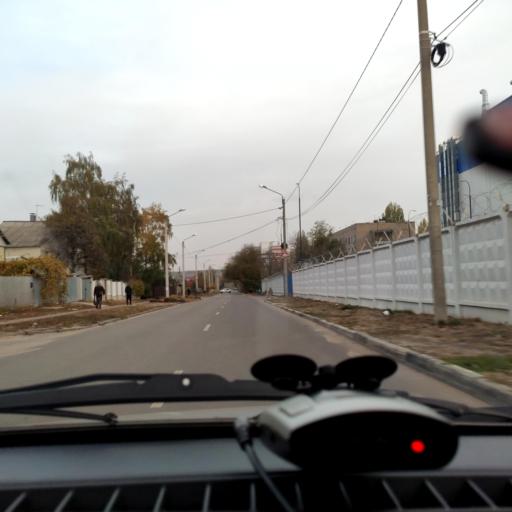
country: RU
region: Voronezj
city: Pridonskoy
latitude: 51.6595
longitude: 39.1263
